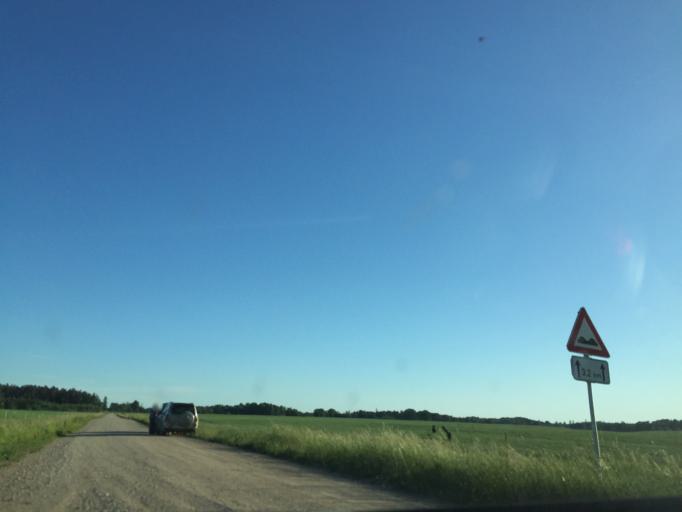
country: LV
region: Talsu Rajons
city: Sabile
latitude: 56.8774
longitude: 22.6109
